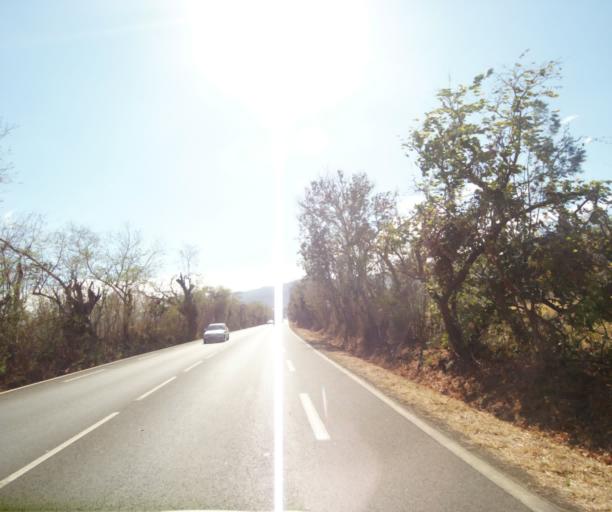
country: RE
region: Reunion
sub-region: Reunion
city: Saint-Paul
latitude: -20.9826
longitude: 55.3050
